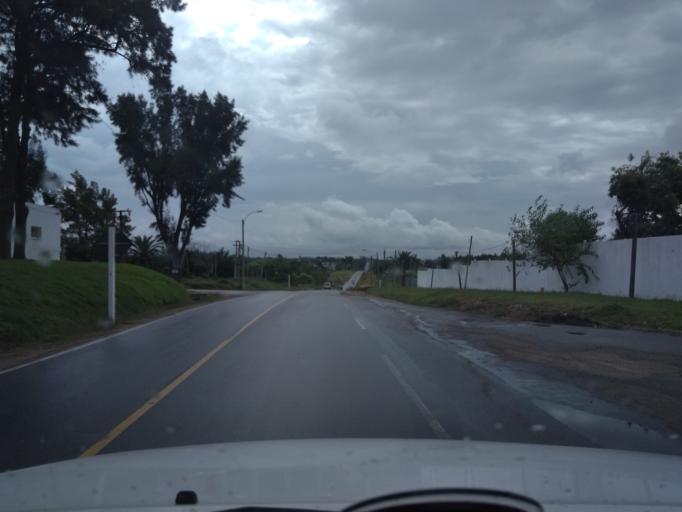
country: UY
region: Canelones
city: Pando
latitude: -34.7107
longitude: -55.9675
